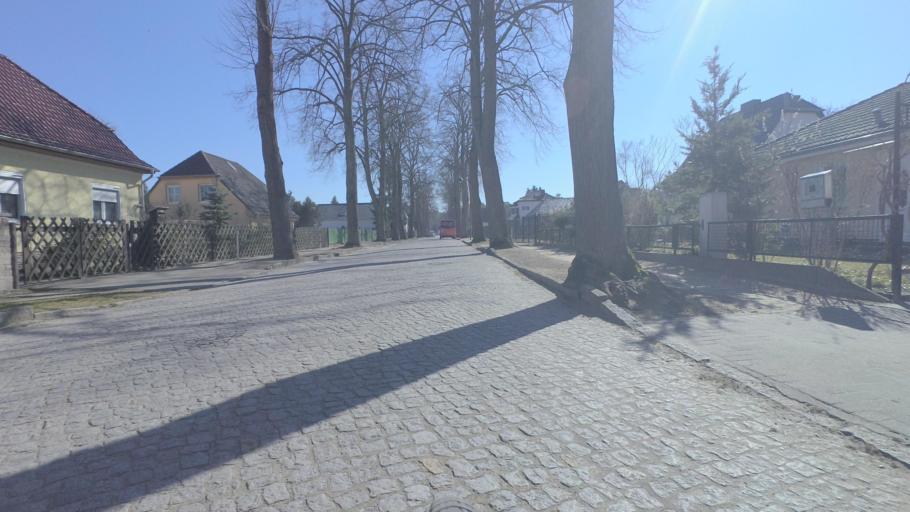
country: DE
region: Brandenburg
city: Rangsdorf
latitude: 52.3204
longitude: 13.4204
